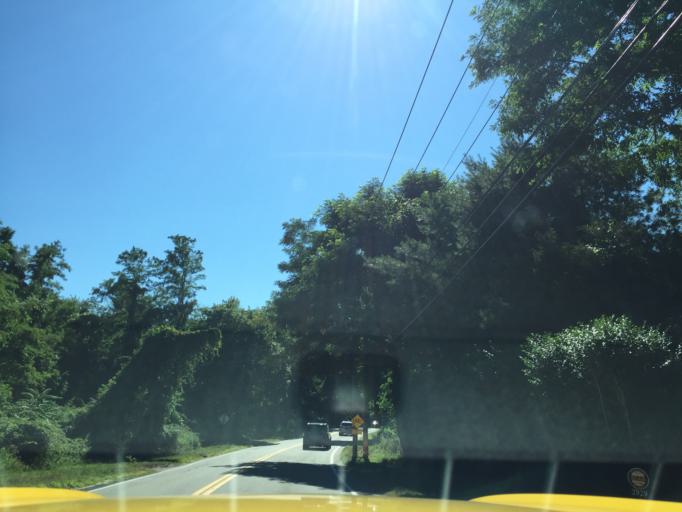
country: US
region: New York
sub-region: Suffolk County
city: Noyack
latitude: 40.9895
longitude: -72.3580
